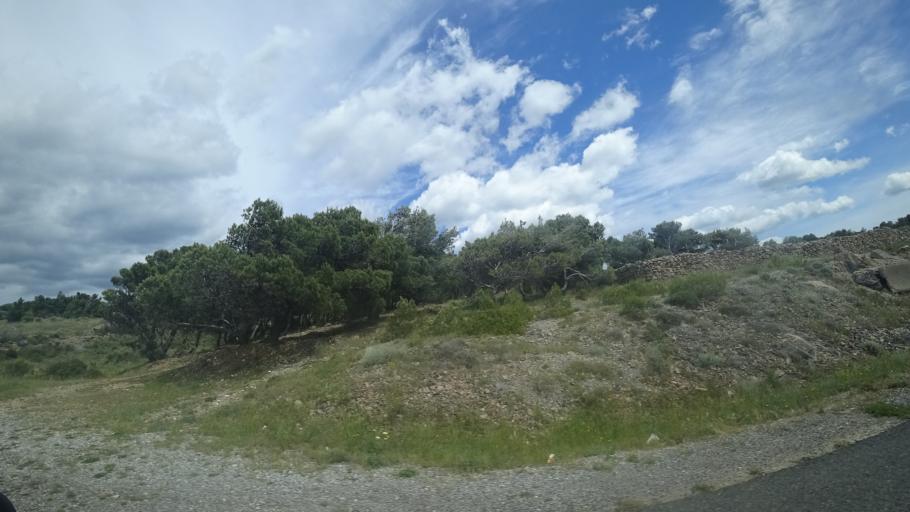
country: FR
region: Languedoc-Roussillon
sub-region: Departement de l'Aude
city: Leucate
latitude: 42.9058
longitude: 3.0200
